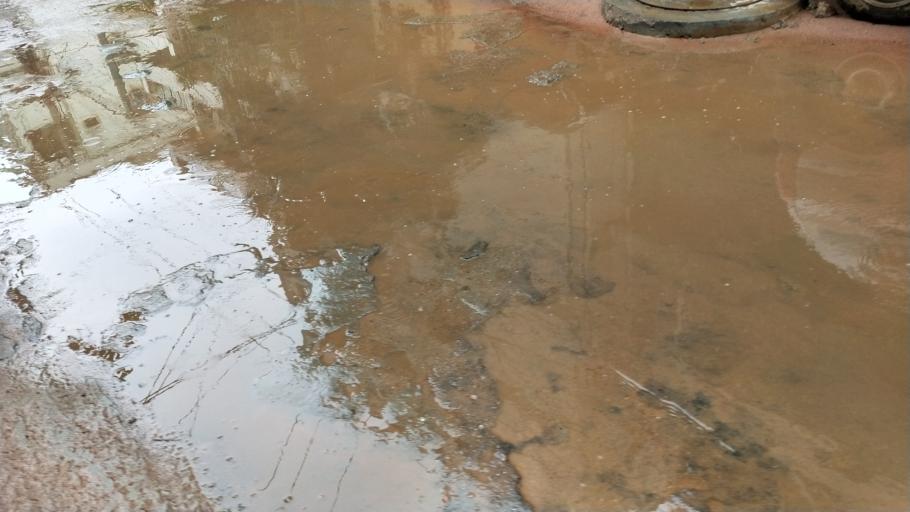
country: IN
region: Telangana
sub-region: Rangareddi
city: Kukatpalli
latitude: 17.4931
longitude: 78.4069
